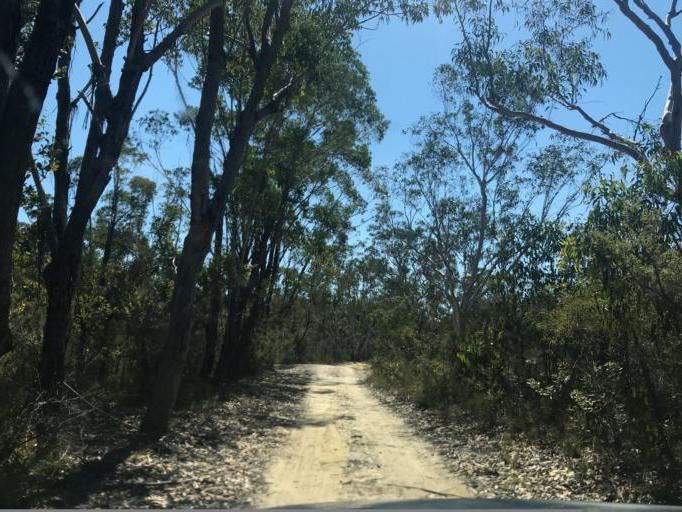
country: AU
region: New South Wales
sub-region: Wyong Shire
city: Little Jilliby
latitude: -33.1551
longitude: 151.0995
